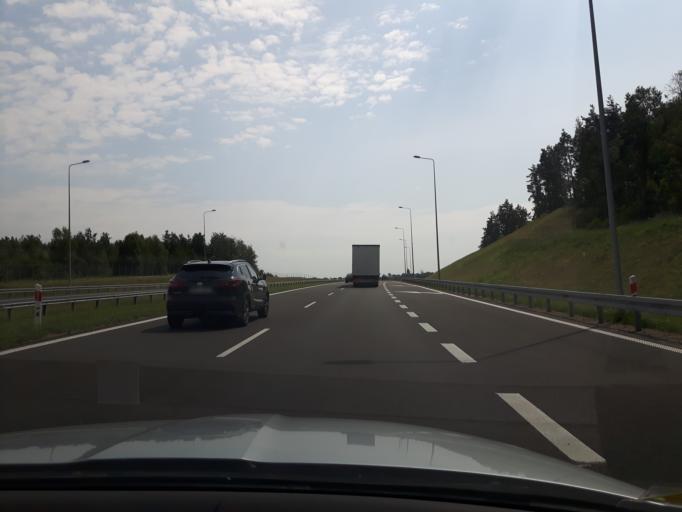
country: PL
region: Warmian-Masurian Voivodeship
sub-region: Powiat nidzicki
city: Nidzica
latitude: 53.3692
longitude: 20.3871
